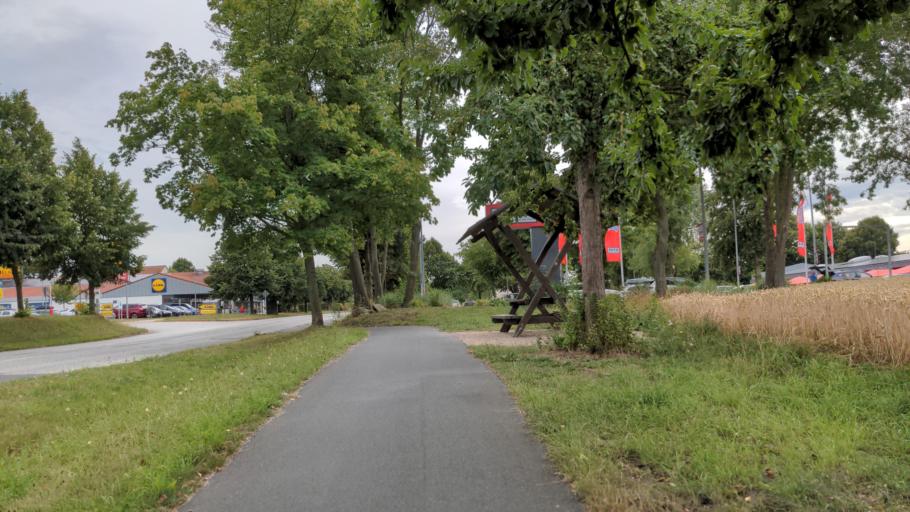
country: DE
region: Mecklenburg-Vorpommern
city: Klutz
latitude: 53.9691
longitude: 11.1722
